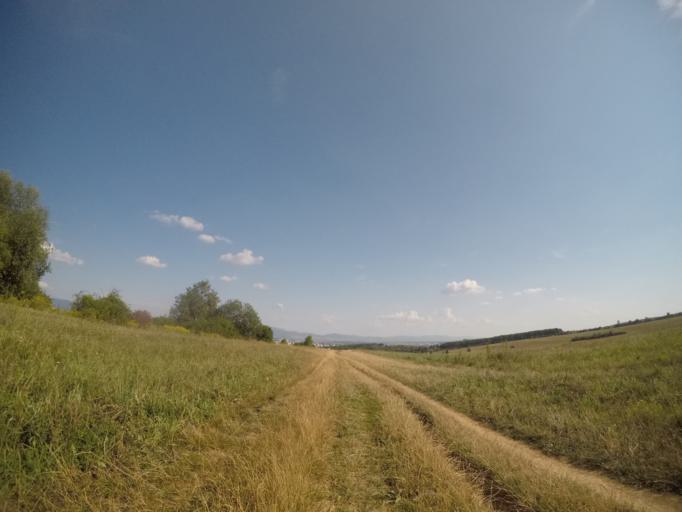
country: SK
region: Kosicky
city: Kosice
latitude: 48.7329
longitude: 21.2133
